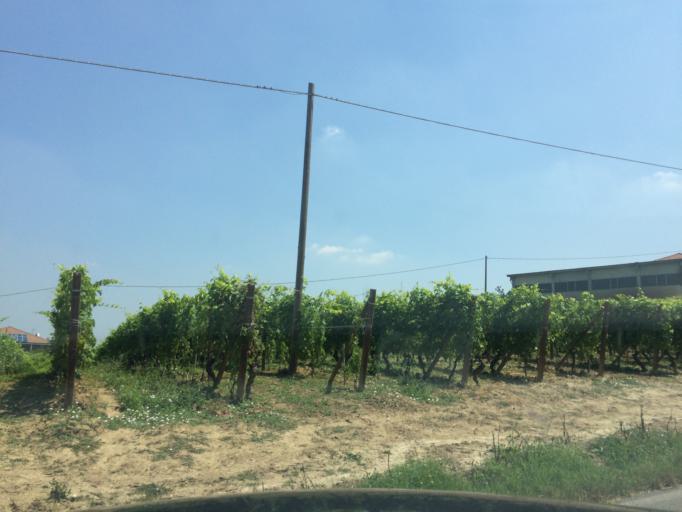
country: IT
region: Piedmont
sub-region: Provincia di Asti
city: Vaglio Serra
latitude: 44.7792
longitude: 8.3223
